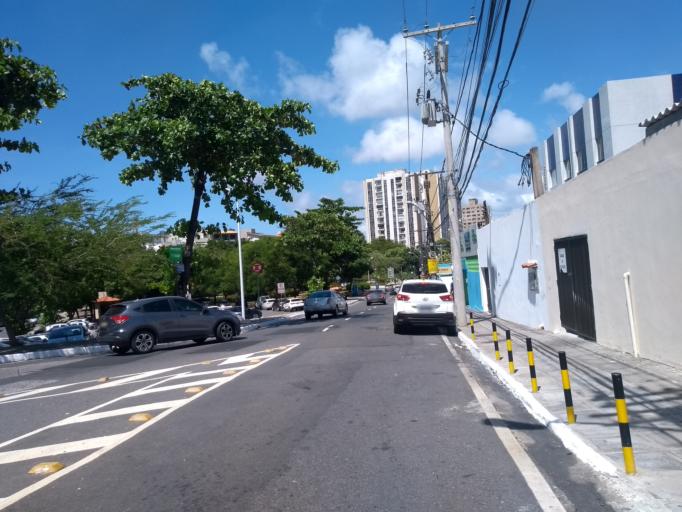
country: BR
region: Bahia
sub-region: Salvador
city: Salvador
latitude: -12.9942
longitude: -38.4585
